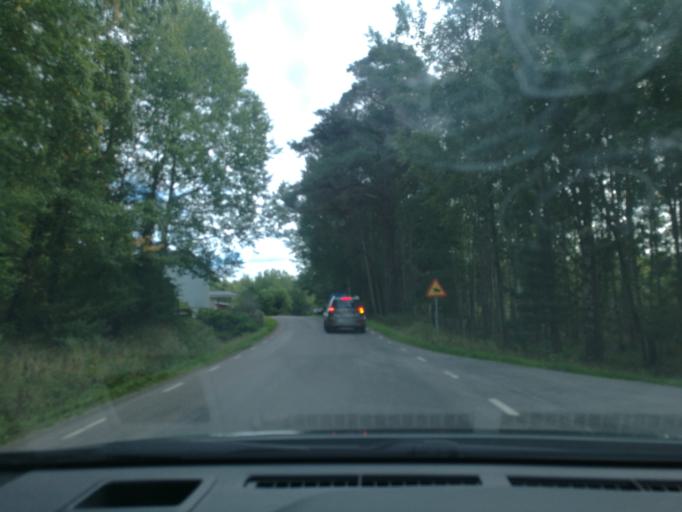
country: SE
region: OEstergoetland
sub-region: Soderkopings Kommun
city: Soederkoeping
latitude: 58.5089
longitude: 16.4319
